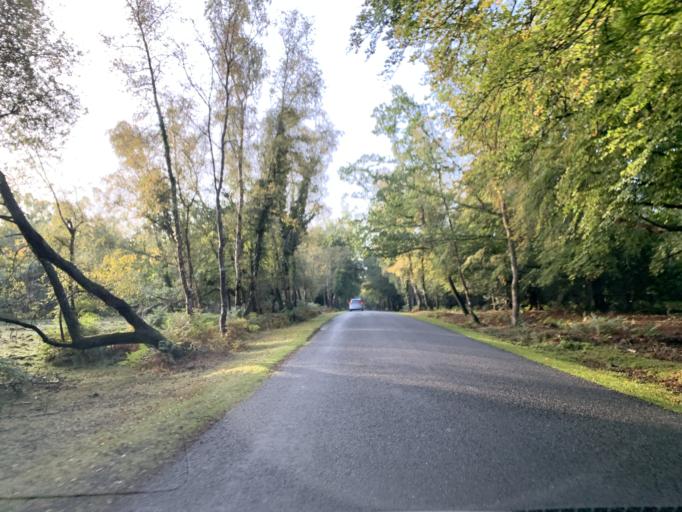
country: GB
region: England
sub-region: Hampshire
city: West Wellow
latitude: 50.9542
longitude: -1.6293
